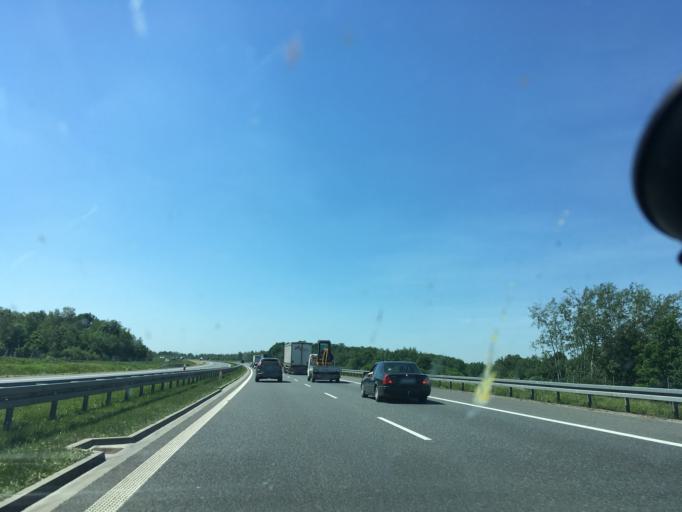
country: PL
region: Lesser Poland Voivodeship
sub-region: Powiat bochenski
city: Borek
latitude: 50.0070
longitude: 20.5362
